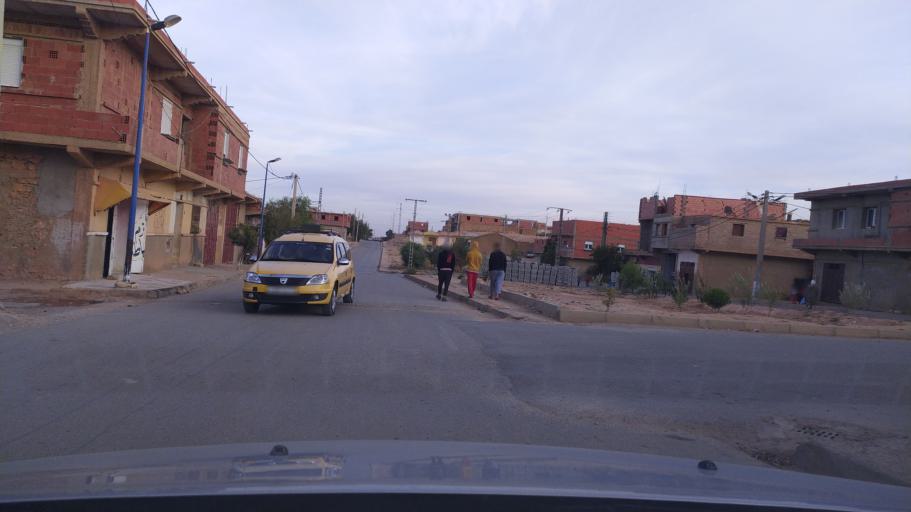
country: DZ
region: Tiaret
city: Frenda
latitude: 34.8936
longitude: 1.2409
